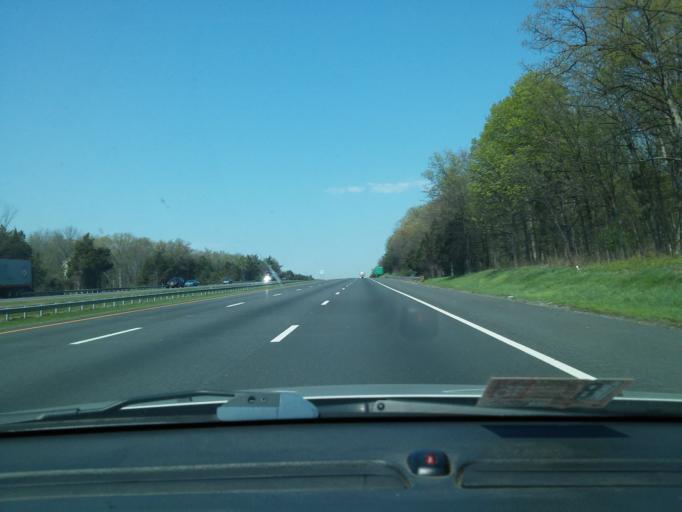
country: US
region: New Jersey
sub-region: Somerset County
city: Bedminster
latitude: 40.6433
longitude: -74.6905
